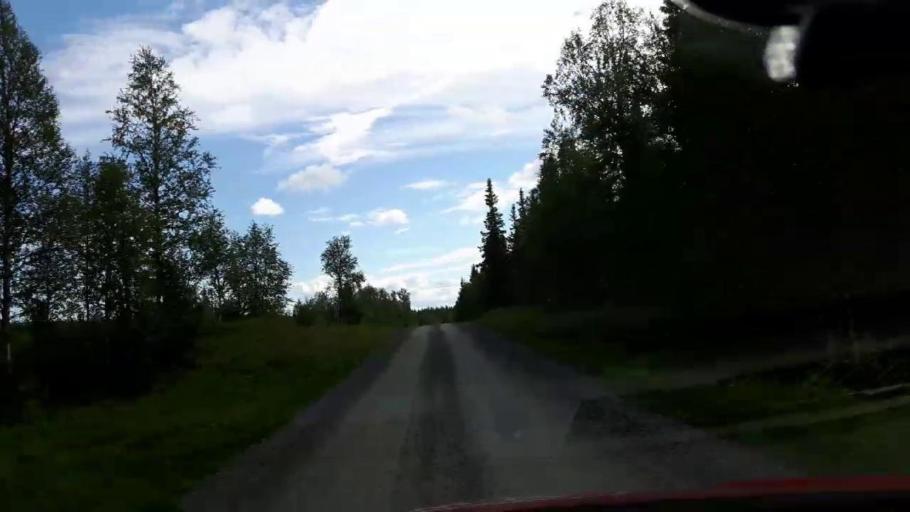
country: SE
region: Jaemtland
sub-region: Krokoms Kommun
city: Valla
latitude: 63.8730
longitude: 14.1223
